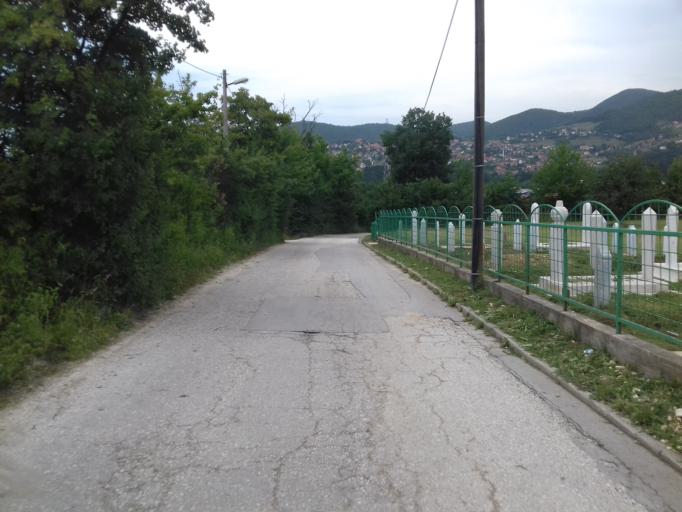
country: BA
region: Federation of Bosnia and Herzegovina
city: Hotonj
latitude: 43.8934
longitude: 18.3625
